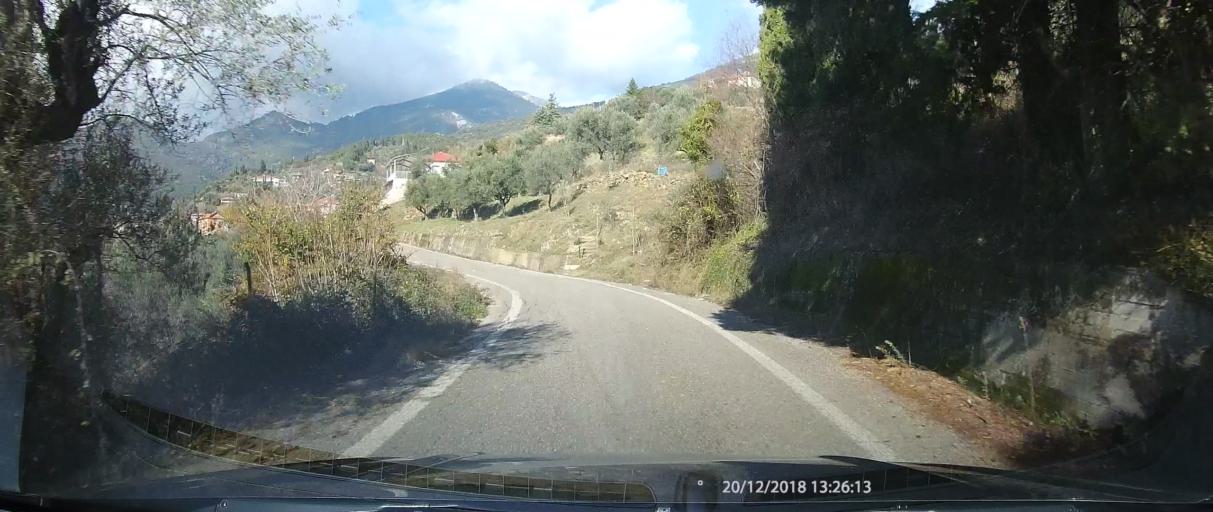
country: GR
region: West Greece
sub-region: Nomos Aitolias kai Akarnanias
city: Paravola
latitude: 38.6279
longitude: 21.5648
